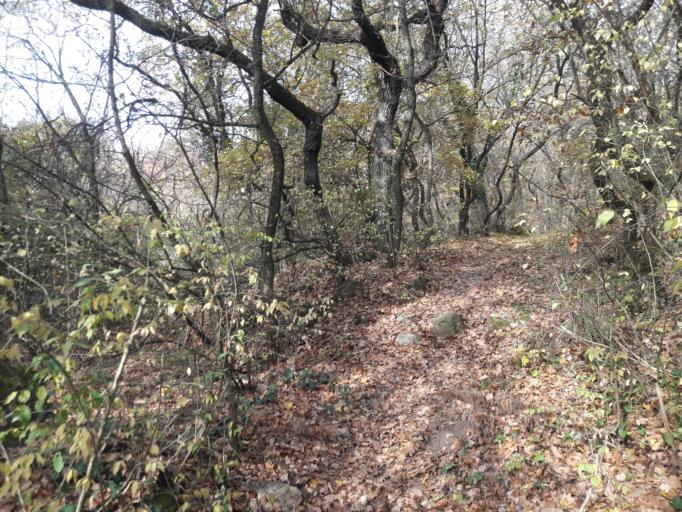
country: HU
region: Pest
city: Budaors
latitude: 47.4742
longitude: 18.9767
